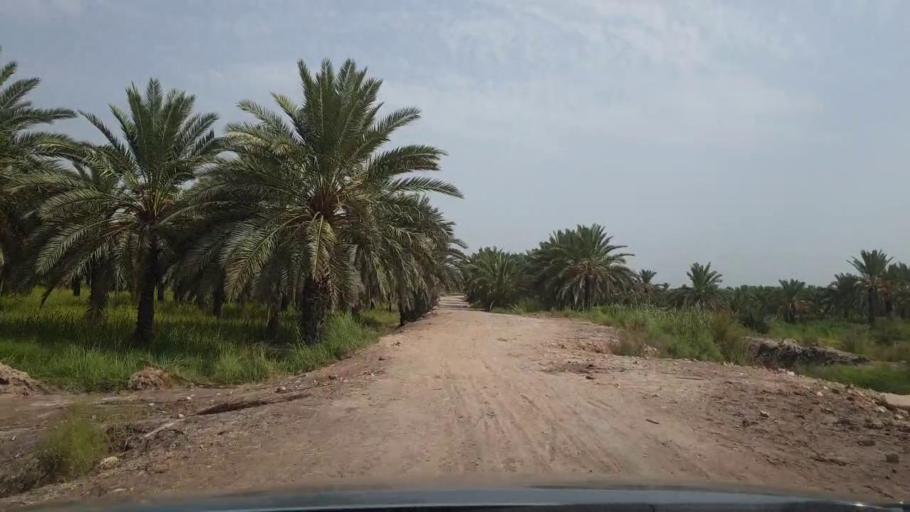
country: PK
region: Sindh
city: Rohri
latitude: 27.6794
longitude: 69.0355
